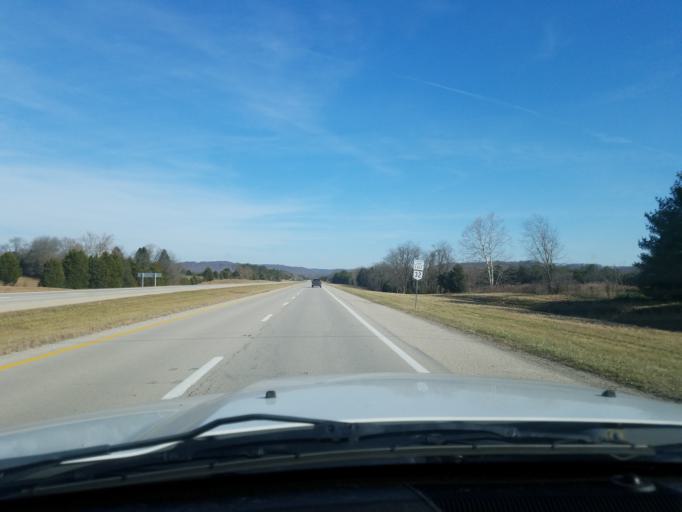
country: US
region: Ohio
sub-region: Adams County
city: Peebles
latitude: 38.9597
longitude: -83.3587
